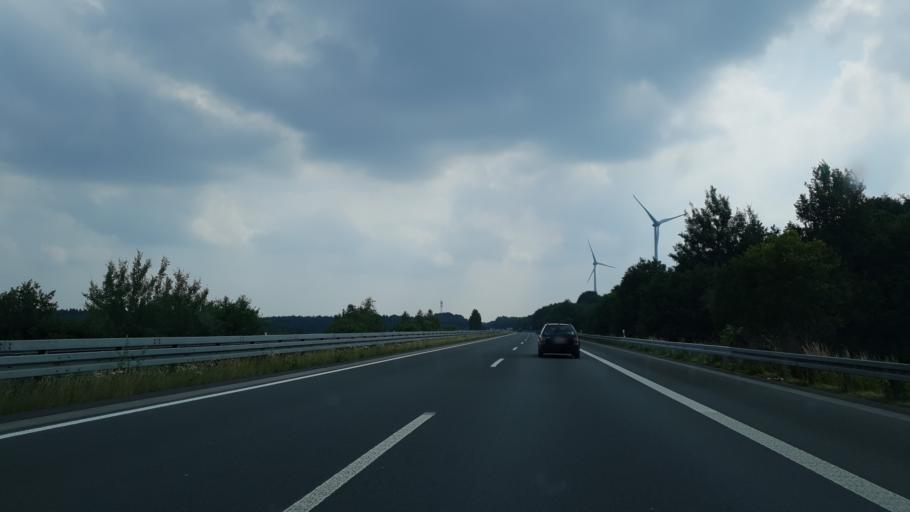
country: DE
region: North Rhine-Westphalia
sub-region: Regierungsbezirk Munster
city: Heiden
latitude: 51.7959
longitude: 6.9744
